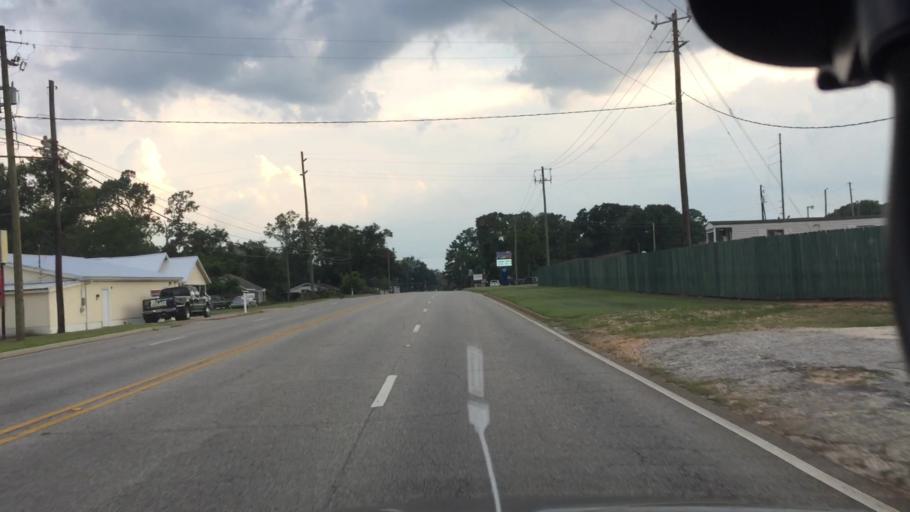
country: US
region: Alabama
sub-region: Coffee County
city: Enterprise
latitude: 31.3205
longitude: -85.8489
